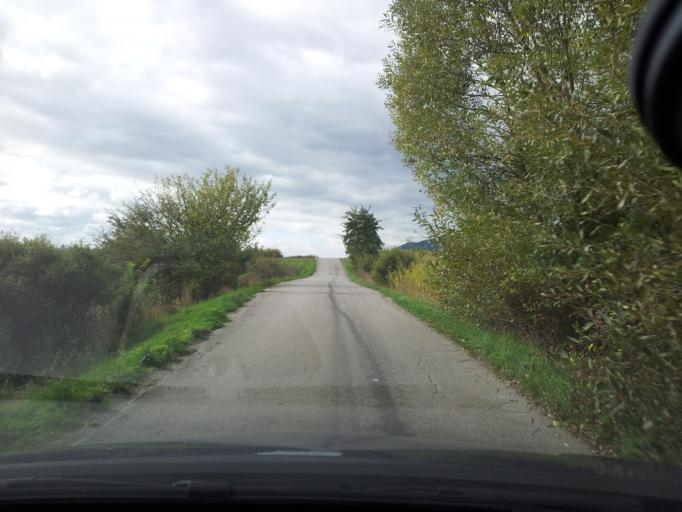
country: SK
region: Zilinsky
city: Ruzomberok
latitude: 49.1056
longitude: 19.4543
